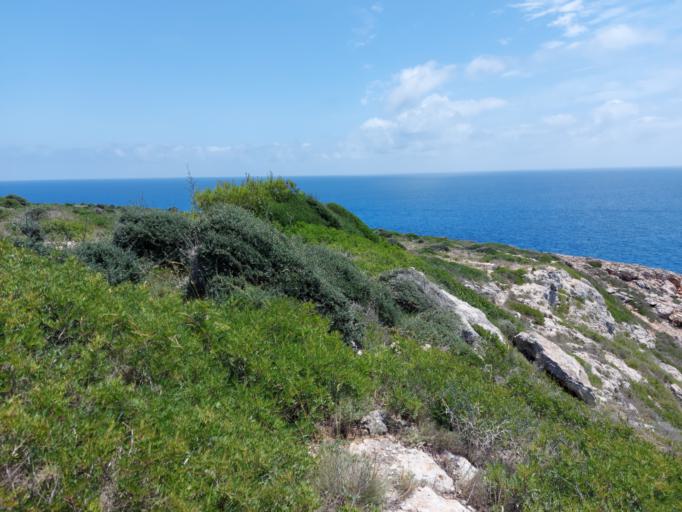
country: ES
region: Balearic Islands
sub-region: Illes Balears
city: Ses Salines
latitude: 39.2895
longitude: 3.0922
